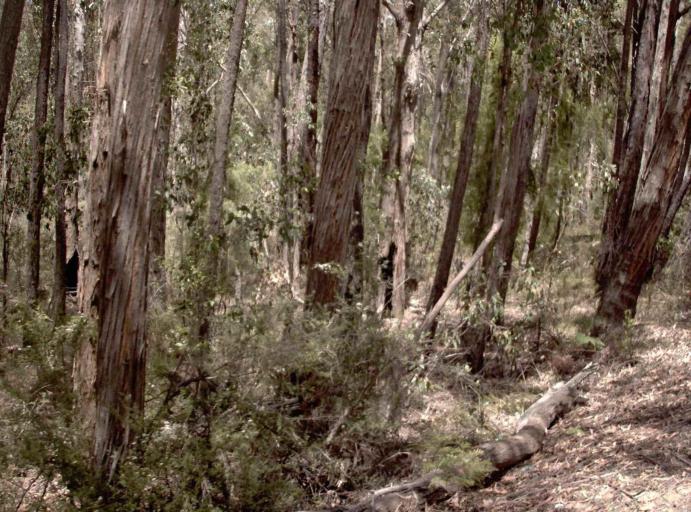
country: AU
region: Victoria
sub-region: East Gippsland
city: Lakes Entrance
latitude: -37.5949
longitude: 147.8919
